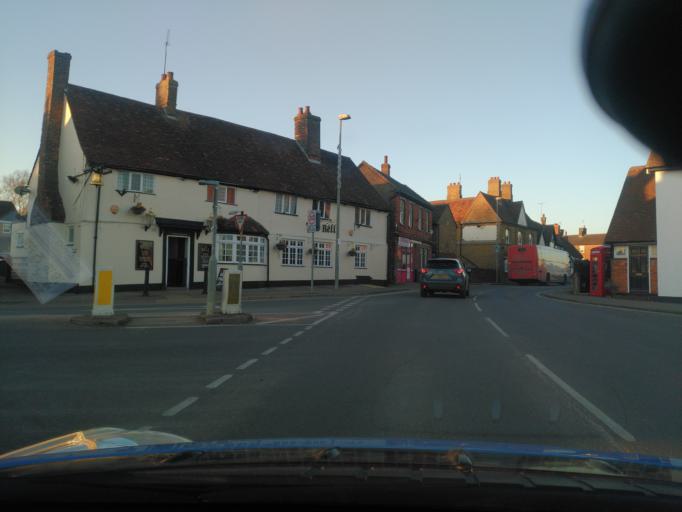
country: GB
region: England
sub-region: Central Bedfordshire
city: Toddington
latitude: 51.9494
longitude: -0.5324
